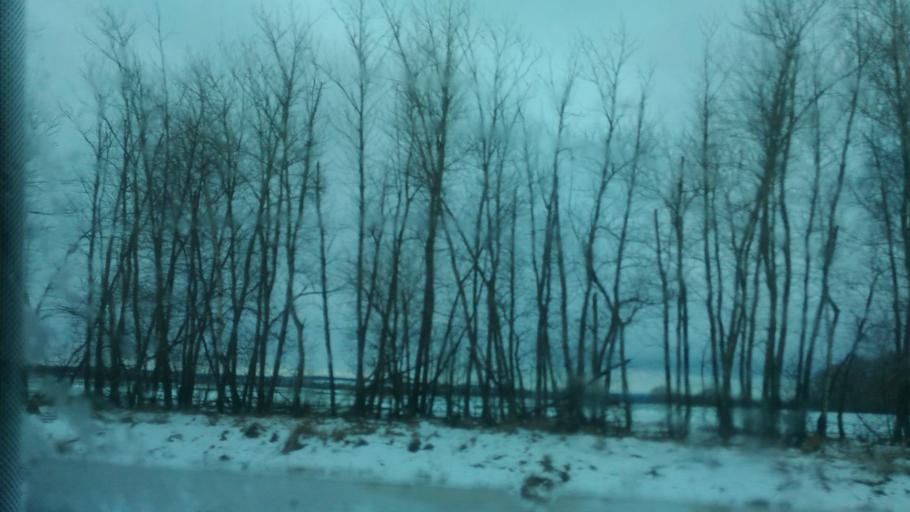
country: RU
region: Tula
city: Bolokhovo
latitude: 54.0801
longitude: 37.7826
